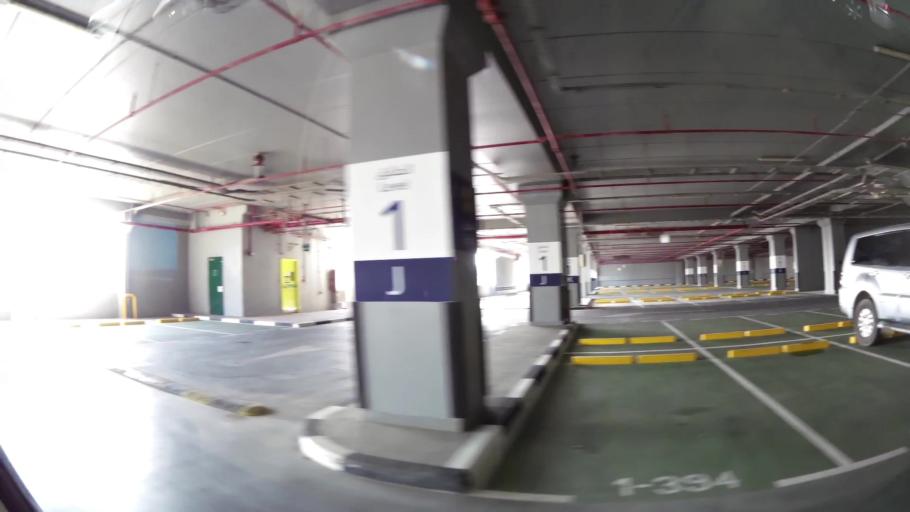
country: AE
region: Ash Shariqah
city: Sharjah
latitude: 25.2536
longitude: 55.4030
